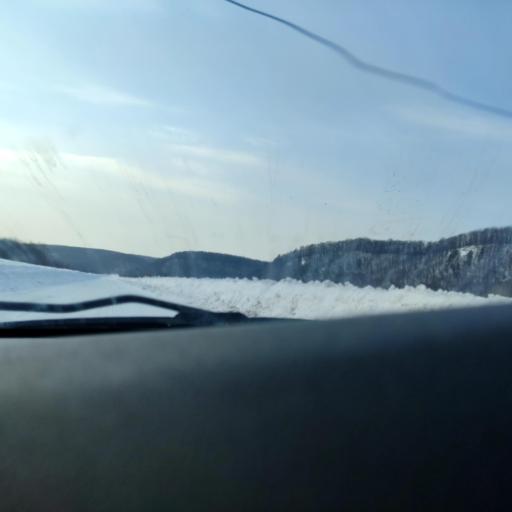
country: RU
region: Samara
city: Novokuybyshevsk
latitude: 53.2426
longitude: 49.8450
